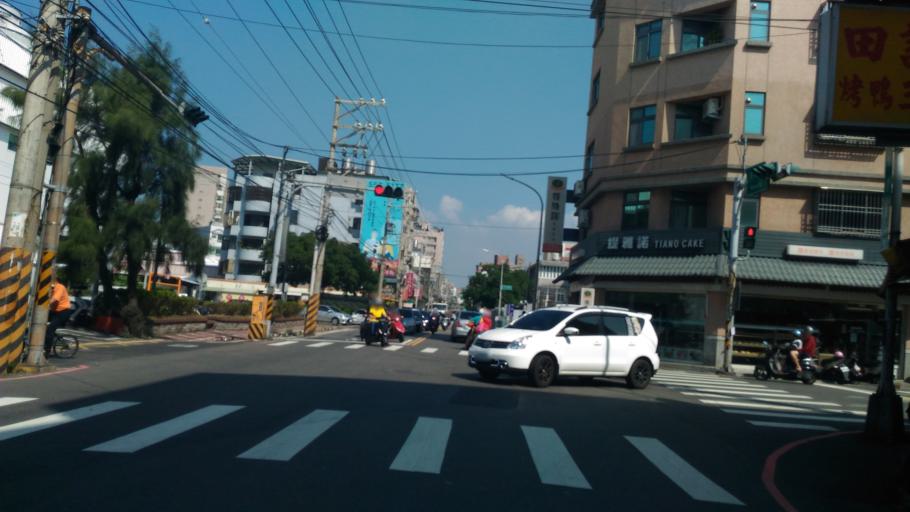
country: TW
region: Taiwan
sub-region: Hsinchu
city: Hsinchu
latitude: 24.8184
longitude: 120.9713
